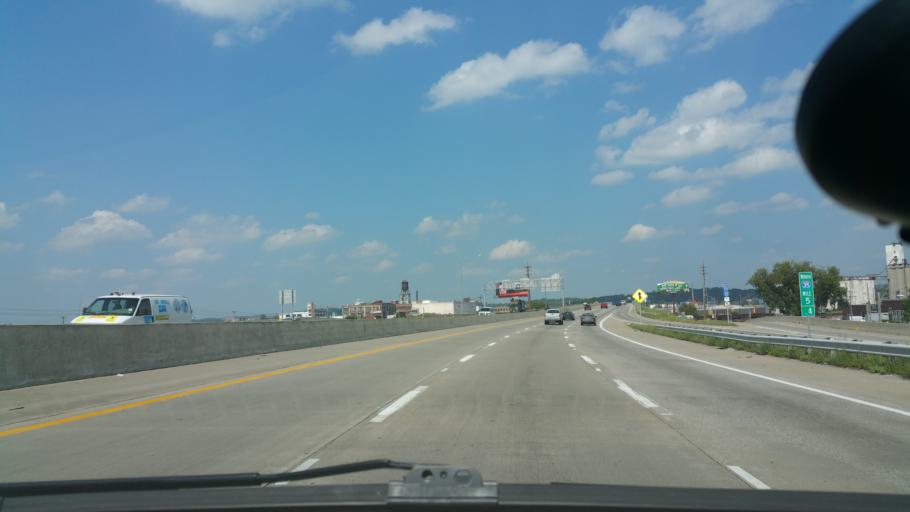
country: US
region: Missouri
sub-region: Clay County
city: North Kansas City
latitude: 39.1277
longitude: -94.5677
